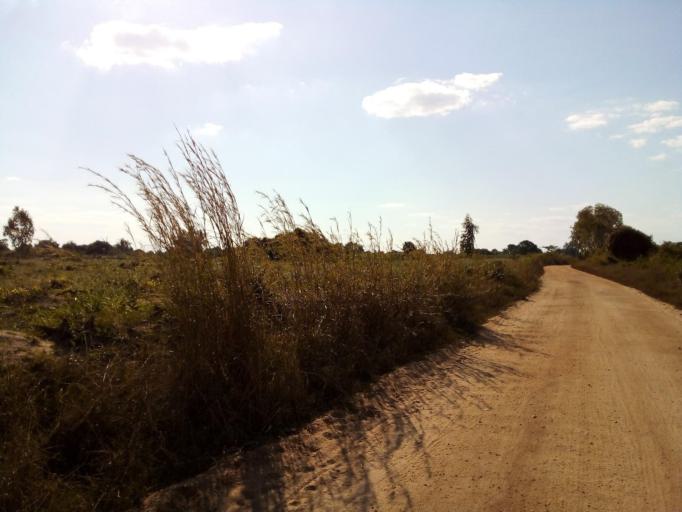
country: MZ
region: Zambezia
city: Quelimane
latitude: -17.5672
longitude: 36.6372
